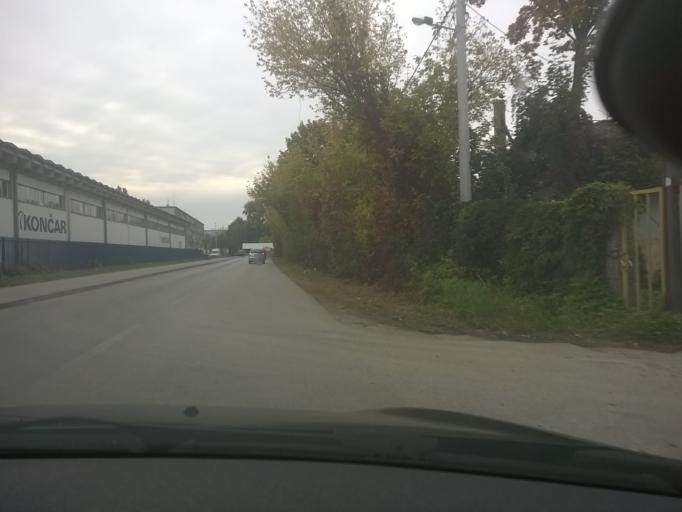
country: HR
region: Grad Zagreb
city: Jankomir
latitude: 45.8060
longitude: 15.9321
